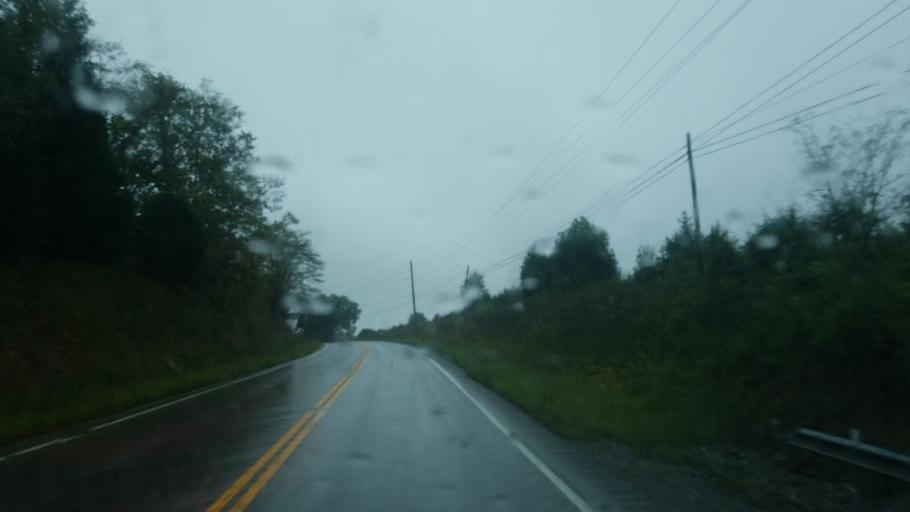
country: US
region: Kentucky
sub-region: Fleming County
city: Flemingsburg
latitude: 38.3594
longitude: -83.6157
